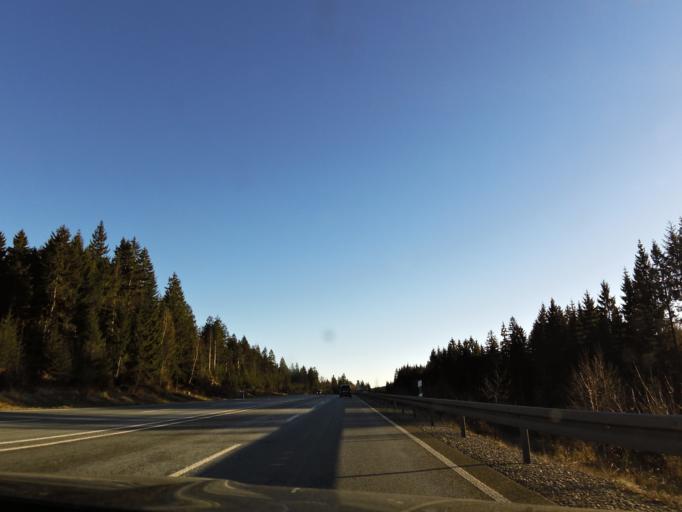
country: DE
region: Bavaria
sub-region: Upper Franconia
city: Fichtelberg
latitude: 50.0466
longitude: 11.8339
